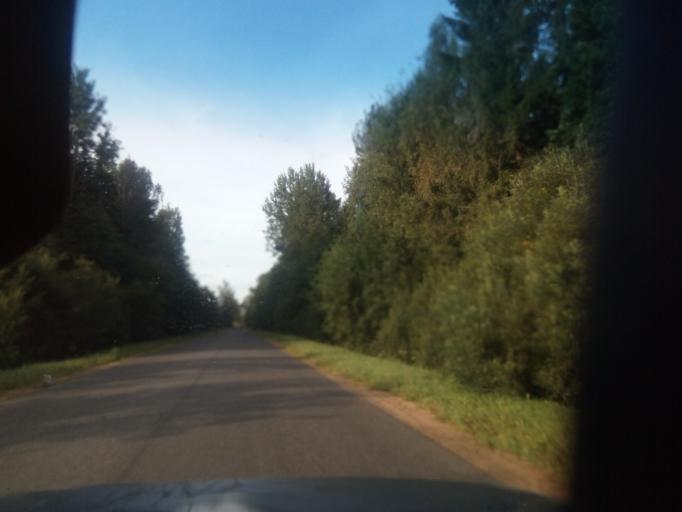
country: BY
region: Vitebsk
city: Dzisna
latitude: 55.6441
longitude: 28.3175
